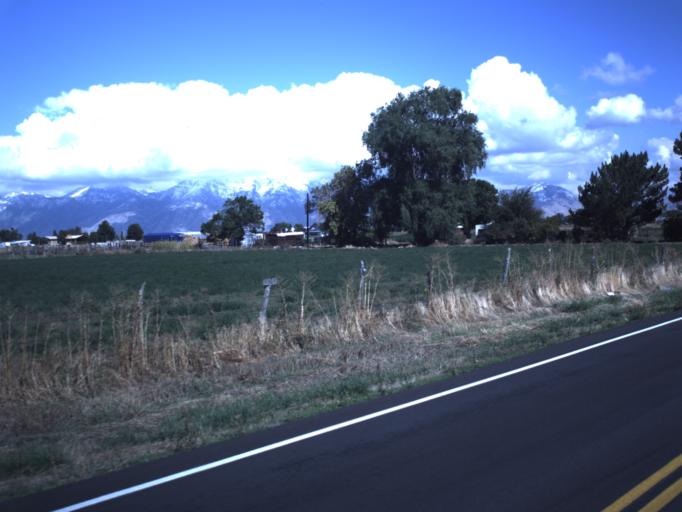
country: US
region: Utah
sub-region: Utah County
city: Benjamin
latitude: 40.0980
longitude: -111.7393
